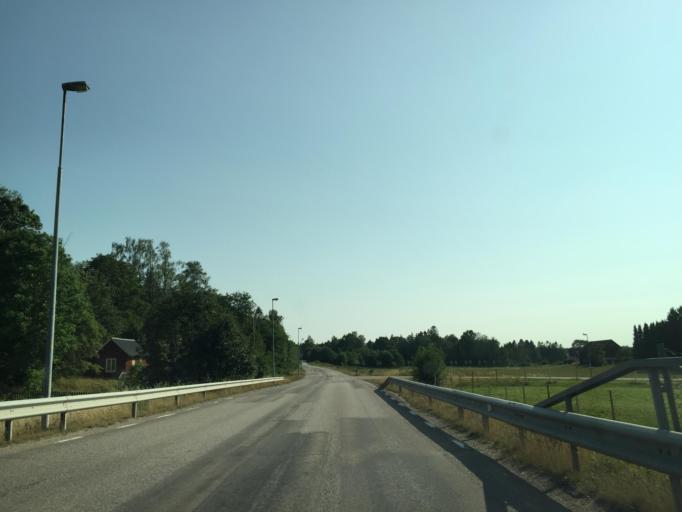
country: SE
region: Vaestra Goetaland
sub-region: Trollhattan
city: Trollhattan
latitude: 58.3256
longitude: 12.2608
